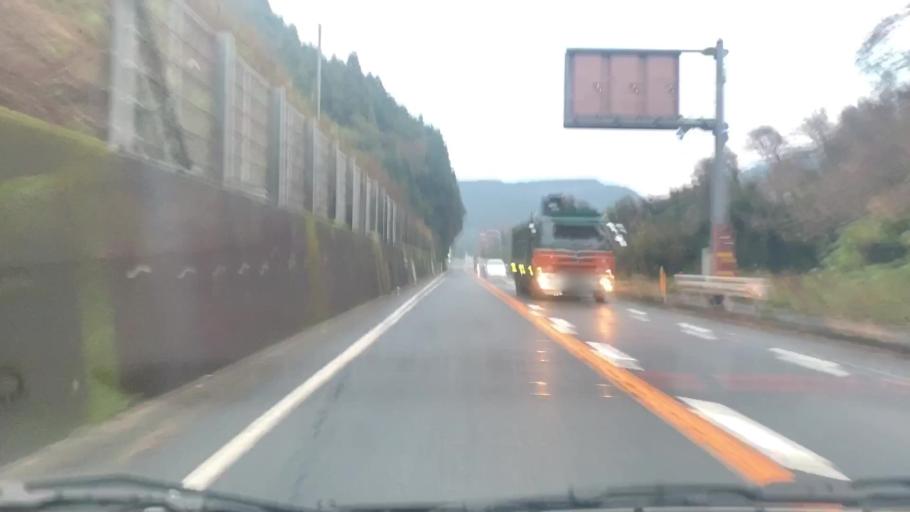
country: JP
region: Saga Prefecture
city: Ureshinomachi-shimojuku
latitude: 33.0782
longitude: 129.9666
